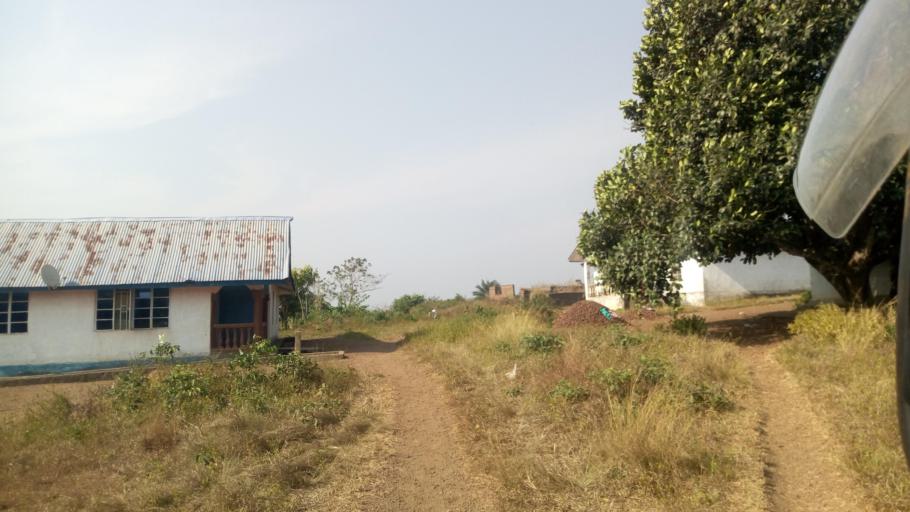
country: SL
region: Southern Province
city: Mogbwemo
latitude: 7.6183
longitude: -12.1808
